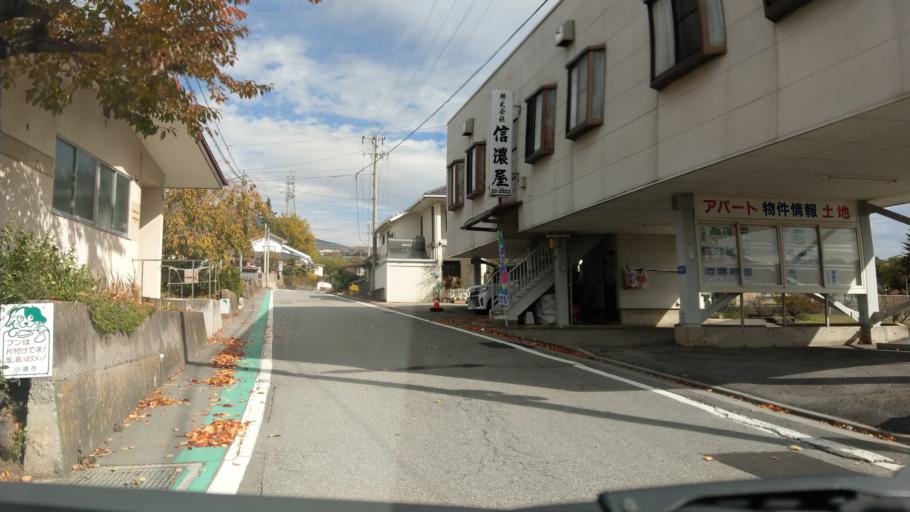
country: JP
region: Nagano
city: Komoro
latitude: 36.3332
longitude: 138.4144
